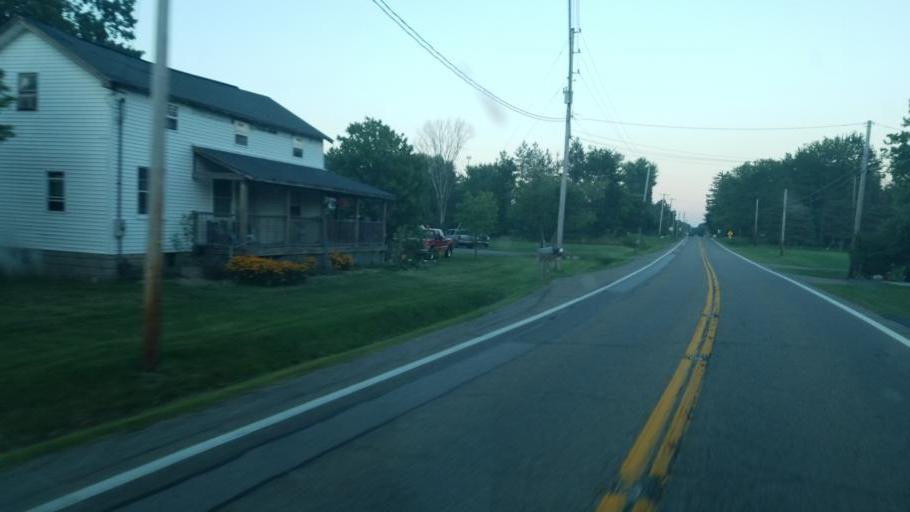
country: US
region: Ohio
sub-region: Trumbull County
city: Champion Heights
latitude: 41.3009
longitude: -80.9032
